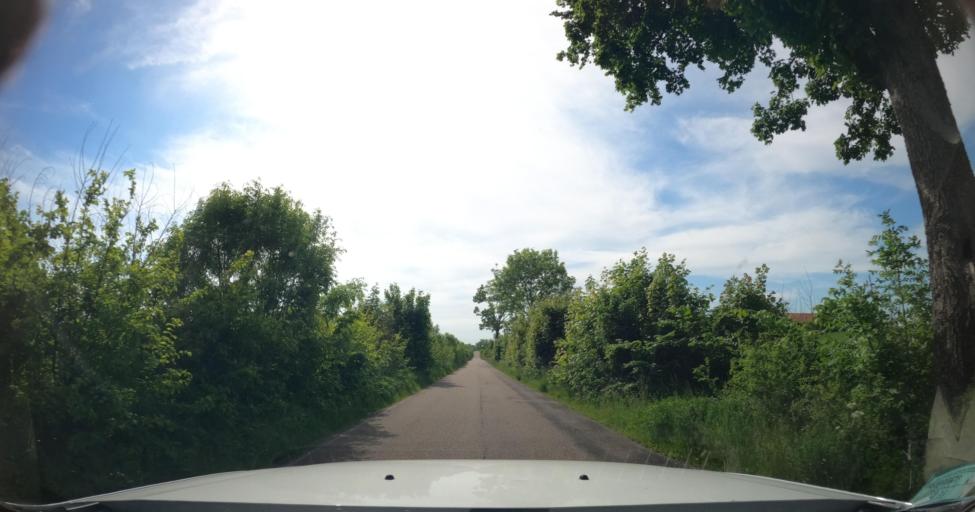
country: PL
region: Warmian-Masurian Voivodeship
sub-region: Powiat ostrodzki
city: Milakowo
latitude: 54.0097
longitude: 20.1294
